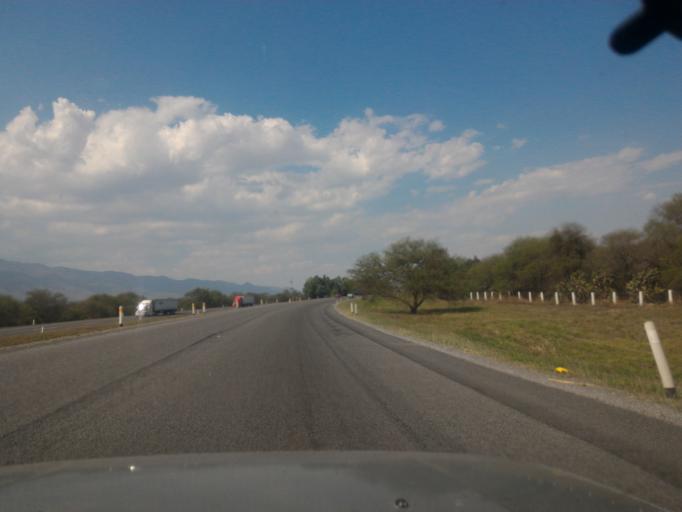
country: MX
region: Jalisco
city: Atoyac
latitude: 19.9905
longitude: -103.5371
